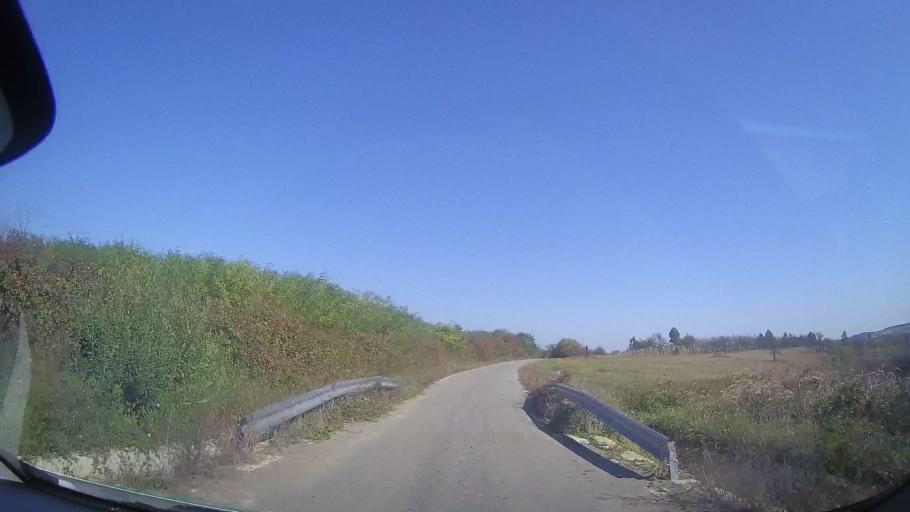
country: RO
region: Timis
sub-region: Comuna Ohaba Lunga
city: Ohaba Lunga
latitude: 45.9142
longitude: 21.9510
